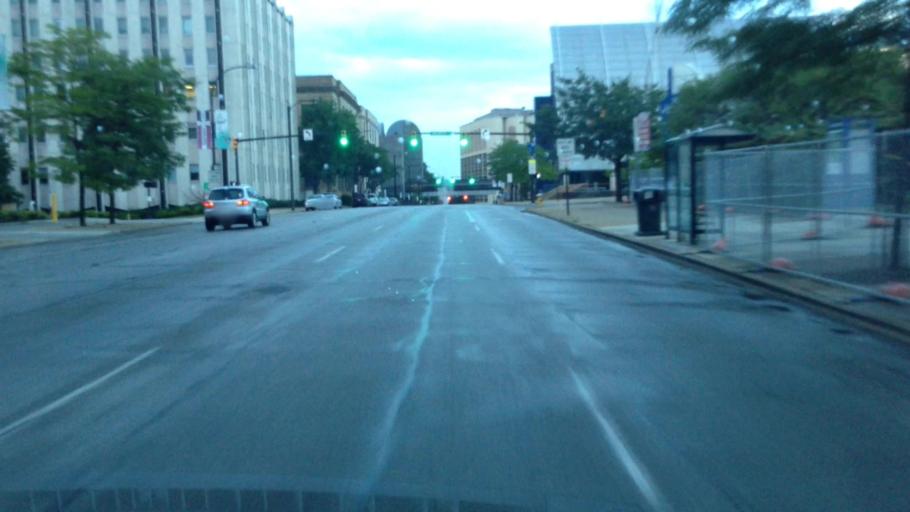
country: US
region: Ohio
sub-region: Summit County
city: Akron
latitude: 41.0779
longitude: -81.5180
